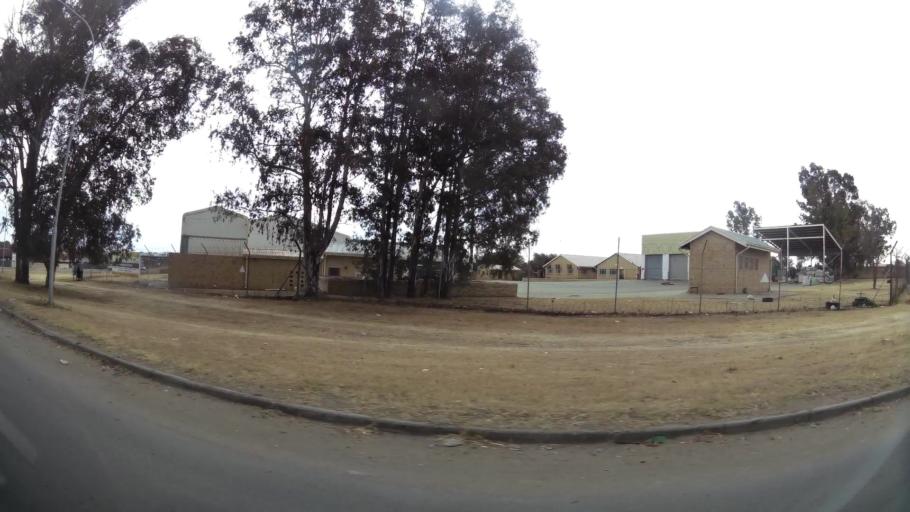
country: ZA
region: Orange Free State
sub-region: Fezile Dabi District Municipality
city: Kroonstad
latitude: -27.6562
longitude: 27.2242
